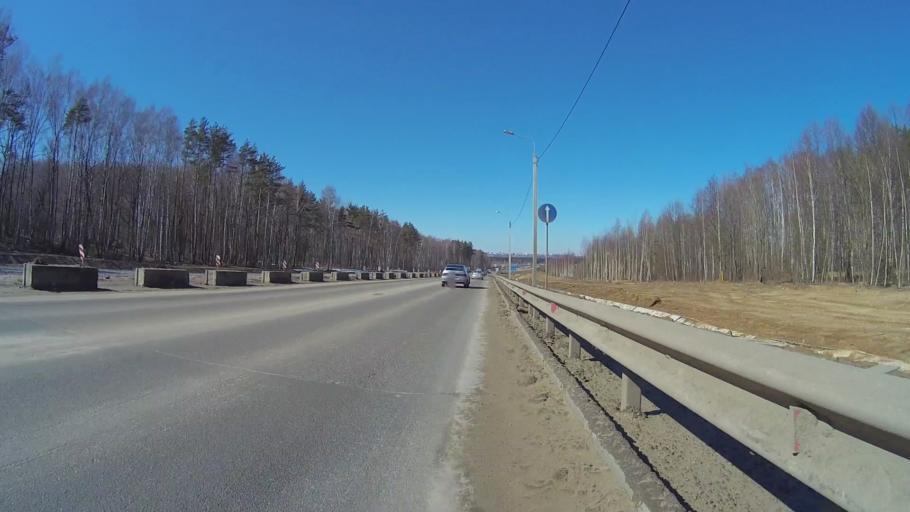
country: RU
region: Vladimir
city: Kommunar
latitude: 56.0738
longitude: 40.4870
